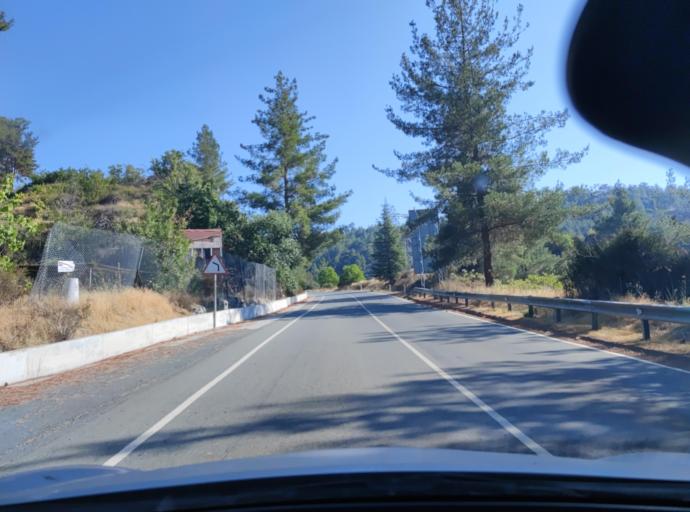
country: CY
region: Limassol
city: Kyperounta
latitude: 34.9280
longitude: 32.9347
